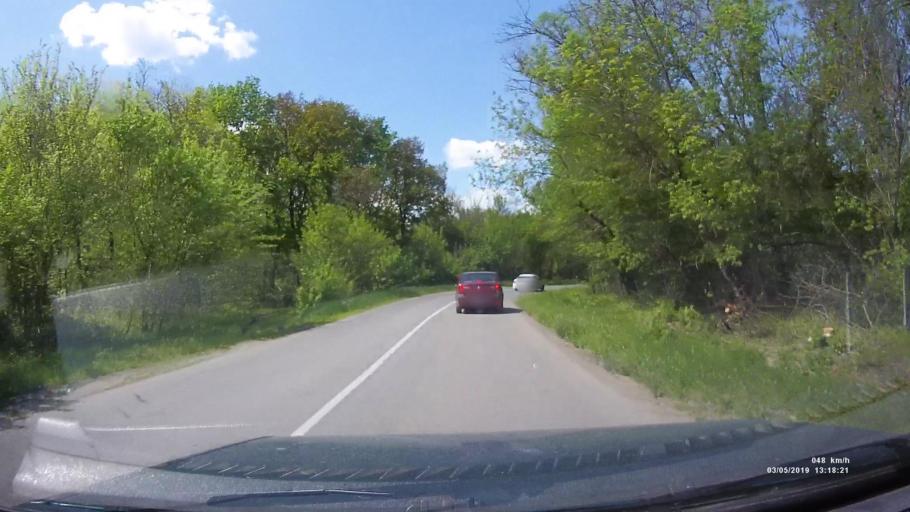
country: RU
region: Rostov
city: Semikarakorsk
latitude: 47.5322
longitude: 40.7487
